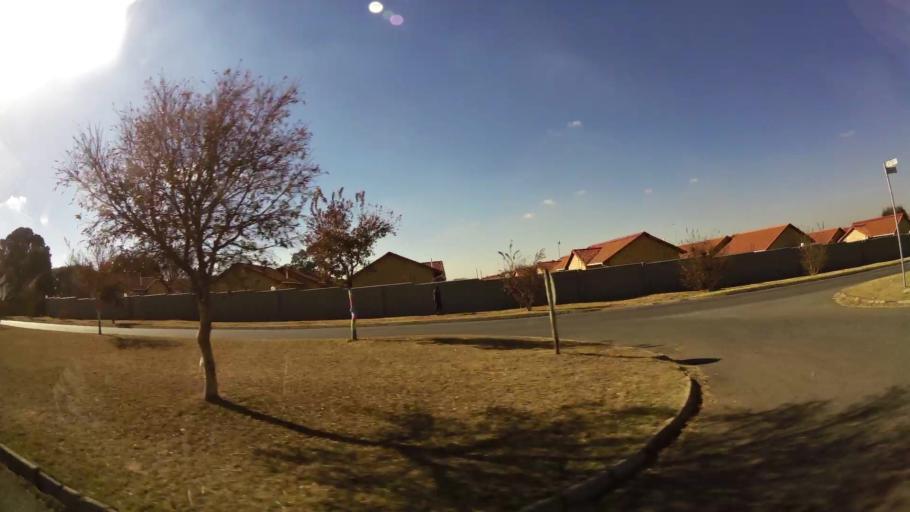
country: ZA
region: Gauteng
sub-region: City of Johannesburg Metropolitan Municipality
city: Roodepoort
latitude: -26.1458
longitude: 27.8343
